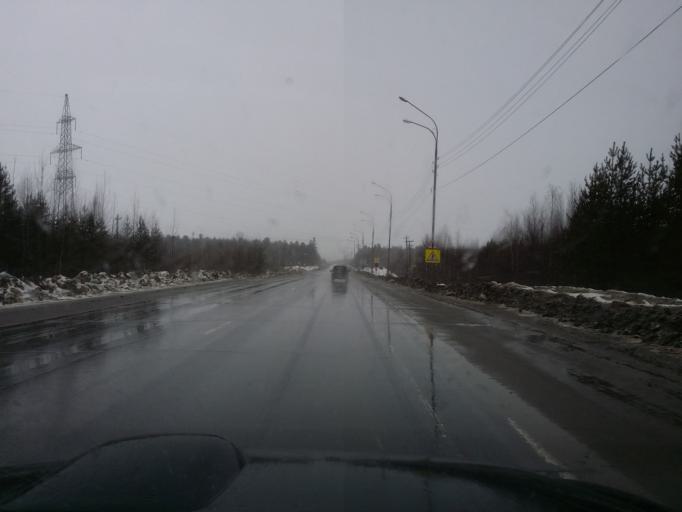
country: RU
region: Khanty-Mansiyskiy Avtonomnyy Okrug
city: Izluchinsk
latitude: 60.9652
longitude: 76.7951
